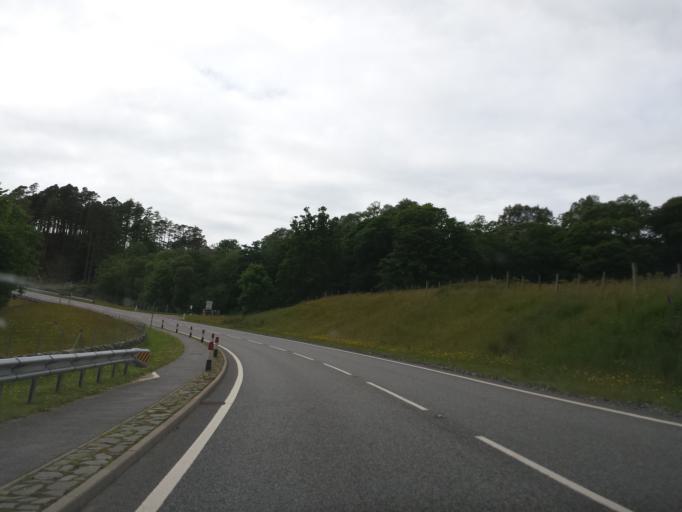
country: GB
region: Scotland
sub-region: Argyll and Bute
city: Isle Of Mull
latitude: 56.8999
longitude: -5.7872
